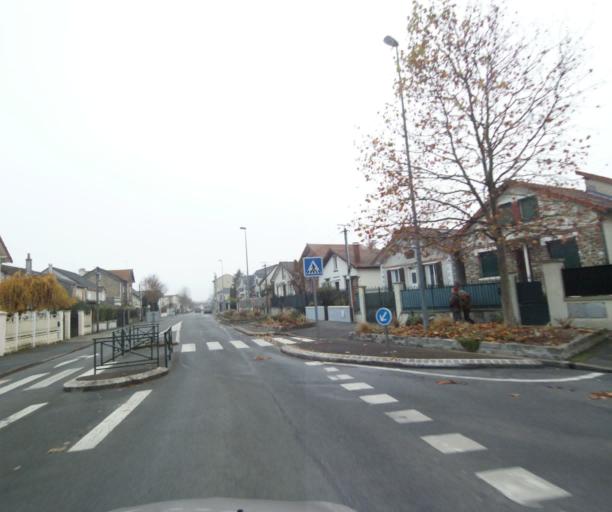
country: FR
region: Ile-de-France
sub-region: Departement du Val-de-Marne
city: Bry-sur-Marne
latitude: 48.8578
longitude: 2.5256
